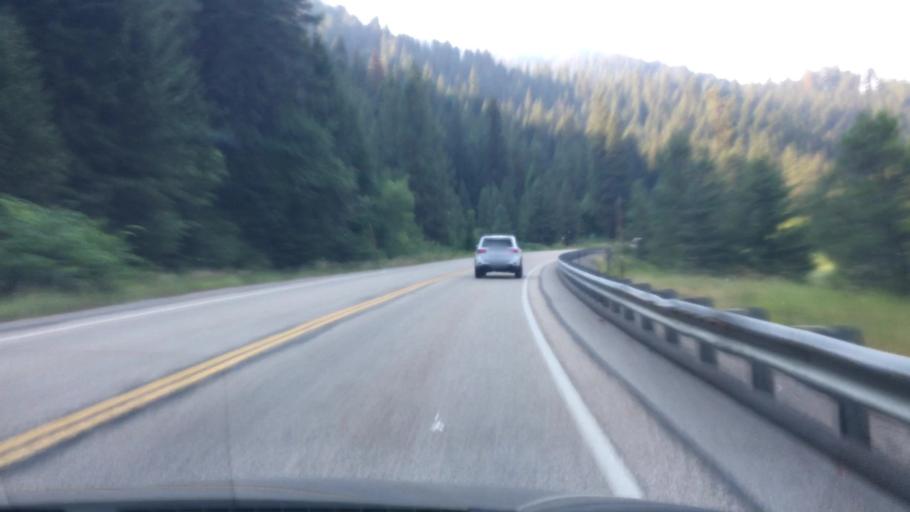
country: US
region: Idaho
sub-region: Valley County
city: Cascade
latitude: 44.1674
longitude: -116.1205
